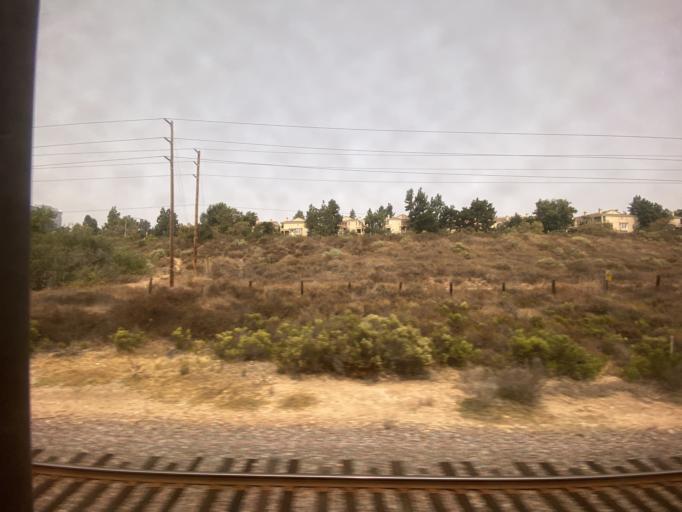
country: US
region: California
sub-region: San Diego County
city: La Jolla
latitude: 32.8632
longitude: -117.2055
